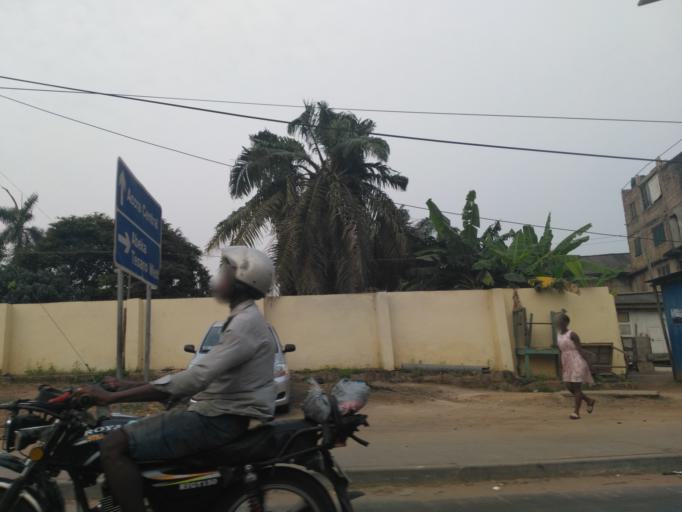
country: GH
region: Greater Accra
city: Dome
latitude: 5.6023
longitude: -0.2256
